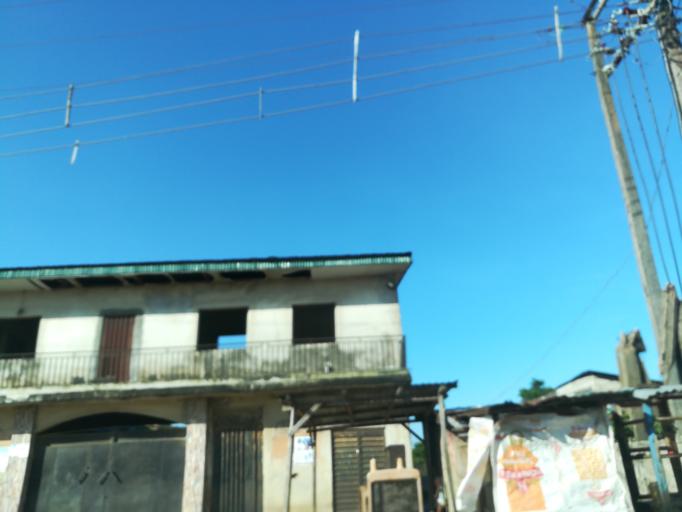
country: NG
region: Lagos
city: Ikorodu
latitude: 6.5387
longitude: 3.5513
